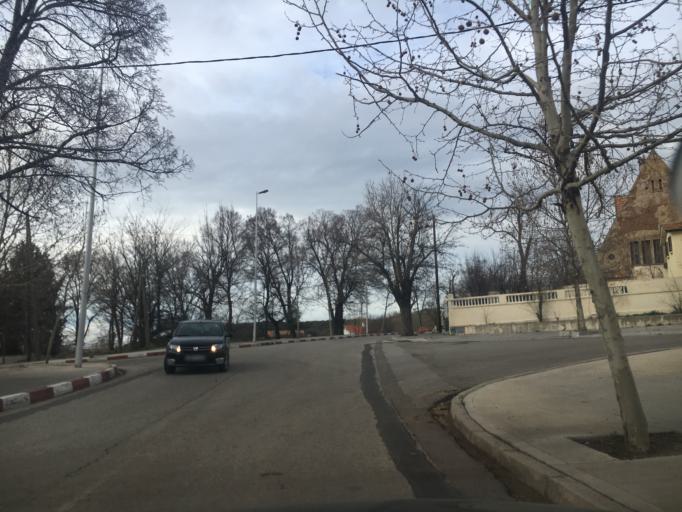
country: MA
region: Meknes-Tafilalet
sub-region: Ifrane
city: Ifrane
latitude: 33.5283
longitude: -5.1124
